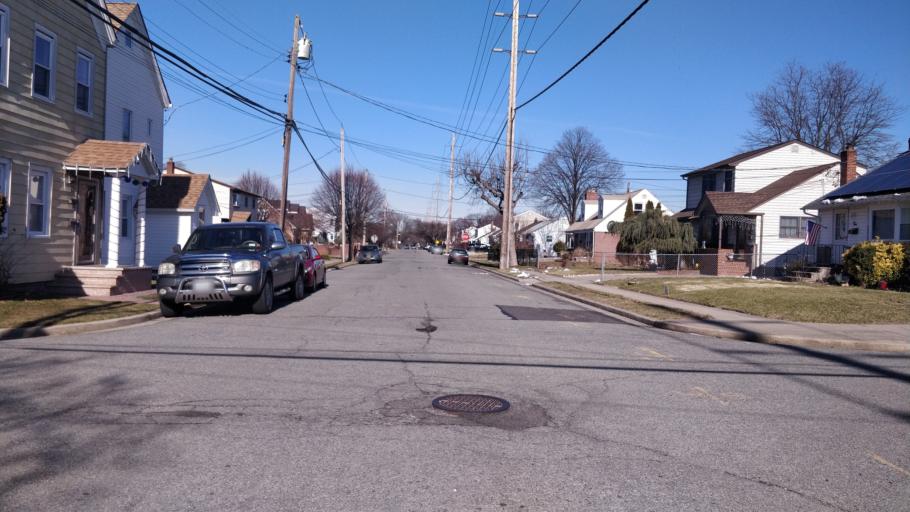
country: US
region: New York
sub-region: Nassau County
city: Hicksville
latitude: 40.7674
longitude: -73.5399
